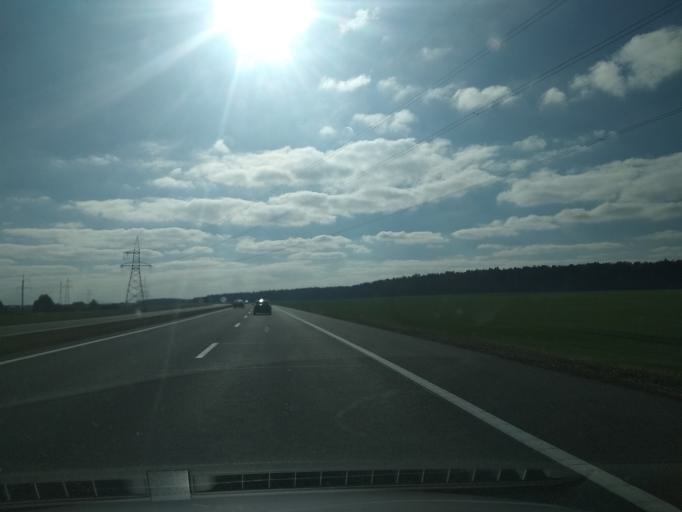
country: BY
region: Brest
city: Baranovichi
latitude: 53.1010
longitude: 25.8870
